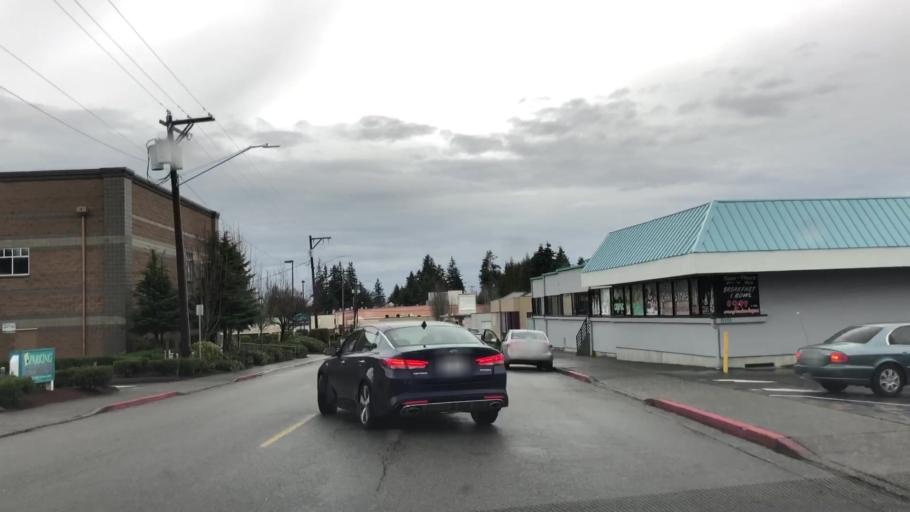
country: US
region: Washington
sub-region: Snohomish County
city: Everett
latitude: 47.9497
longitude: -122.2131
